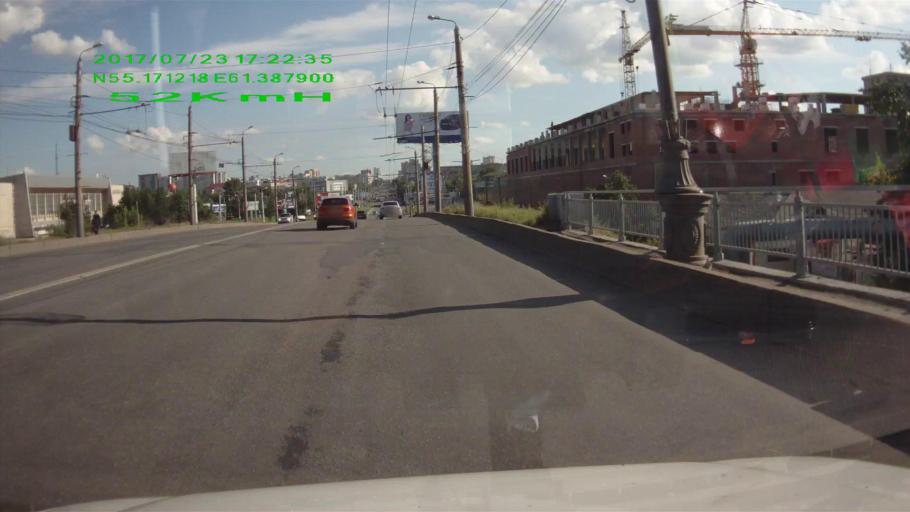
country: RU
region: Chelyabinsk
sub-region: Gorod Chelyabinsk
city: Chelyabinsk
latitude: 55.1707
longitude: 61.3879
